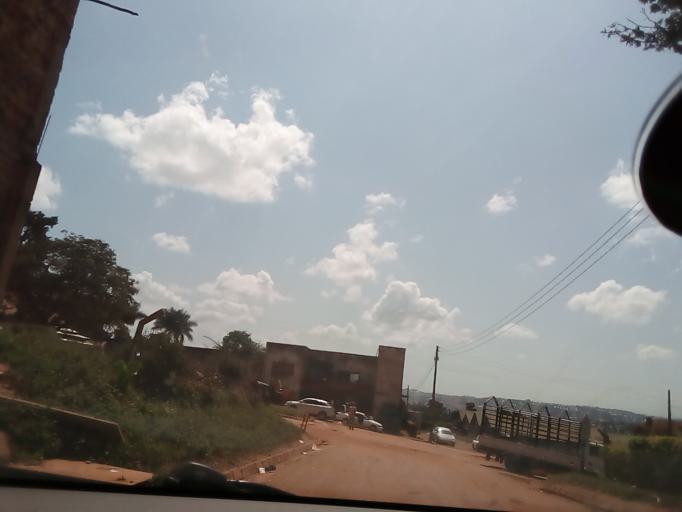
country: UG
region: Central Region
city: Masaka
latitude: -0.3384
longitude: 31.7399
